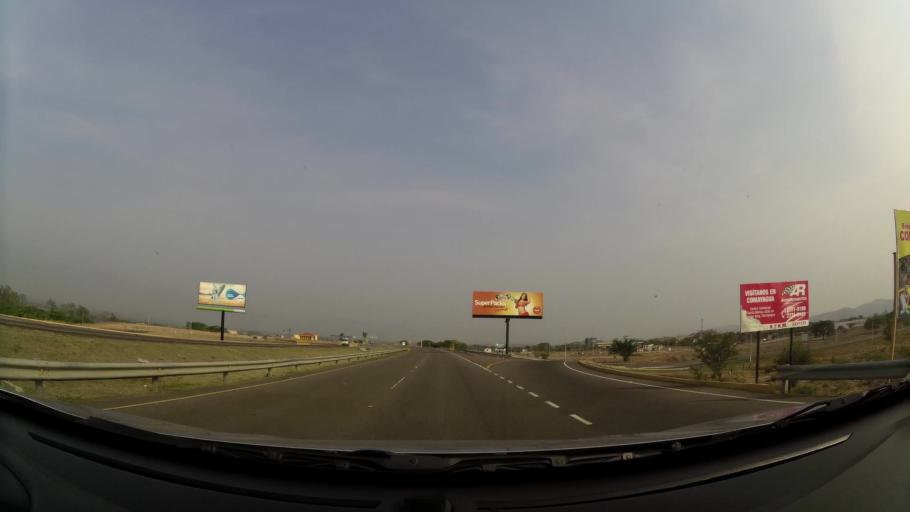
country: HN
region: Comayagua
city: Comayagua
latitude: 14.4234
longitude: -87.6306
